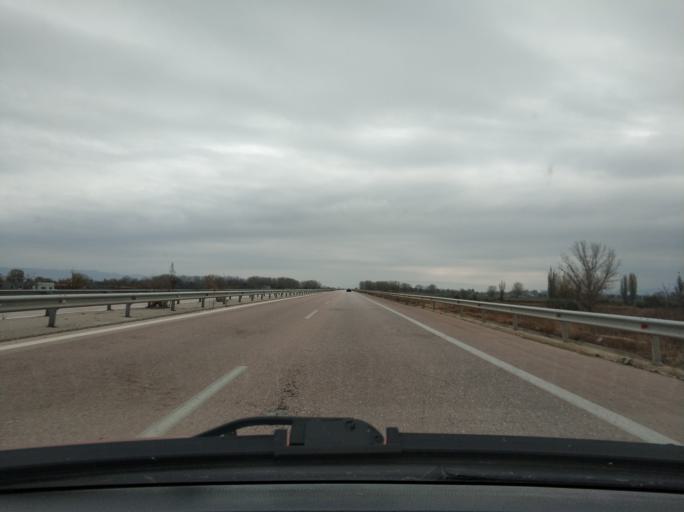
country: GR
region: Central Macedonia
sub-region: Nomos Thessalonikis
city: Kavallari
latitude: 40.7319
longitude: 23.0511
